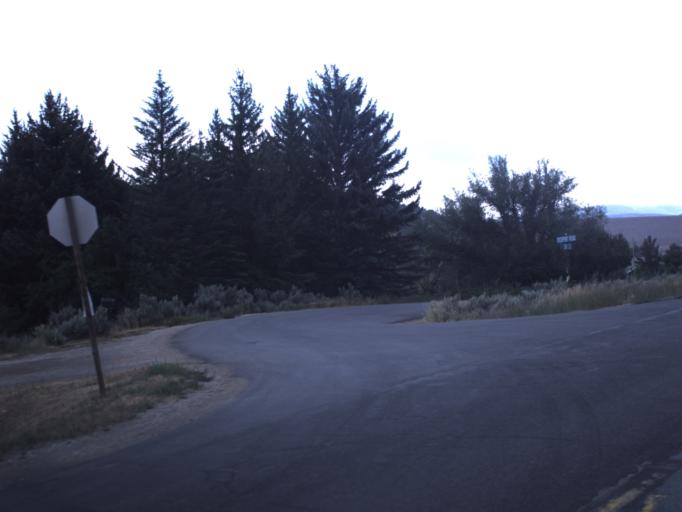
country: US
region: Utah
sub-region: Summit County
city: Coalville
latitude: 40.7988
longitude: -111.4092
